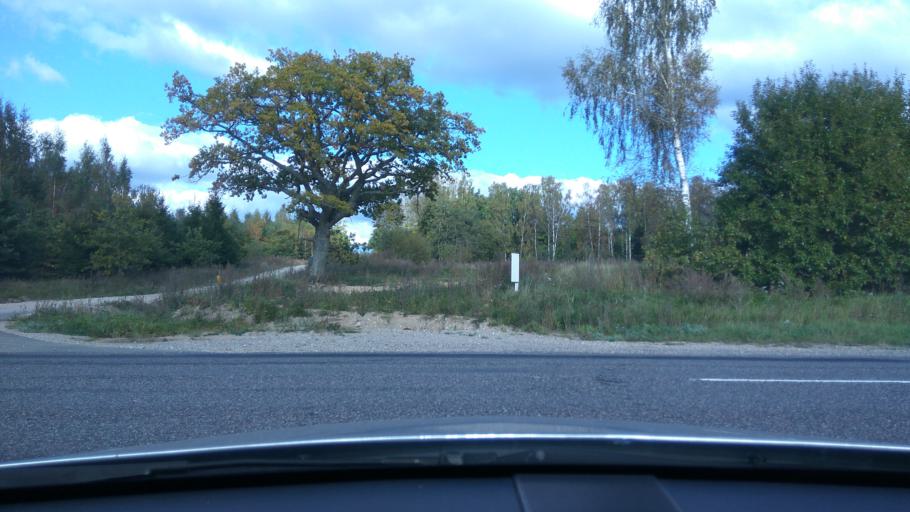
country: LV
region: Kuldigas Rajons
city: Kuldiga
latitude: 57.0265
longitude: 21.8575
